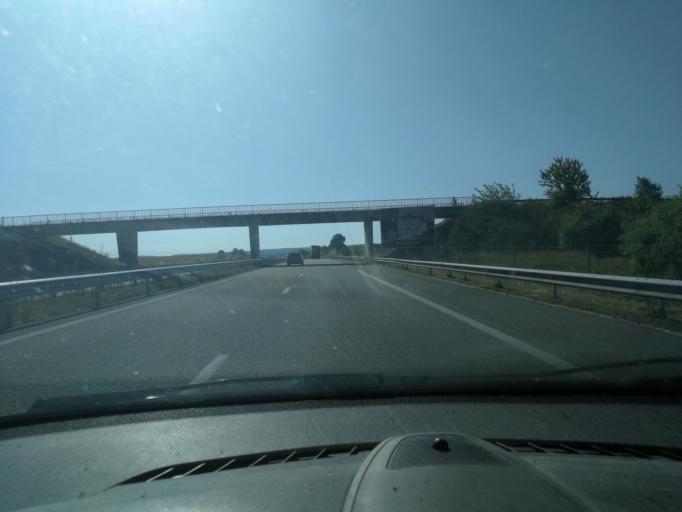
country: FR
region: Alsace
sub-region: Departement du Bas-Rhin
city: Drulingen
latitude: 48.8010
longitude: 7.1855
